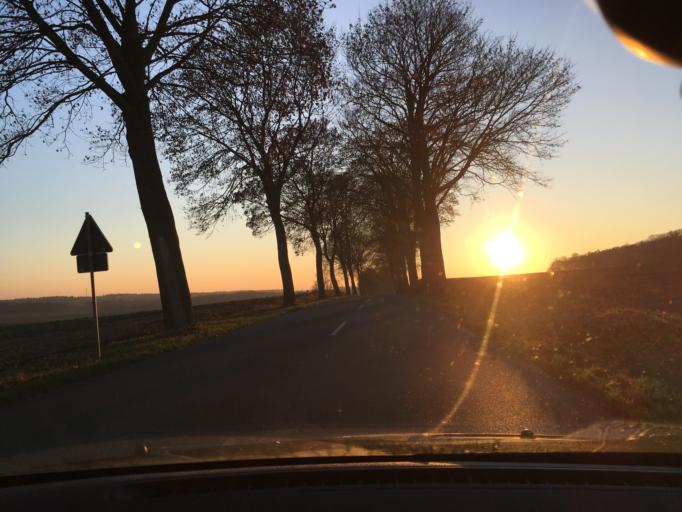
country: DE
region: Lower Saxony
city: Natendorf
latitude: 53.0547
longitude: 10.4492
